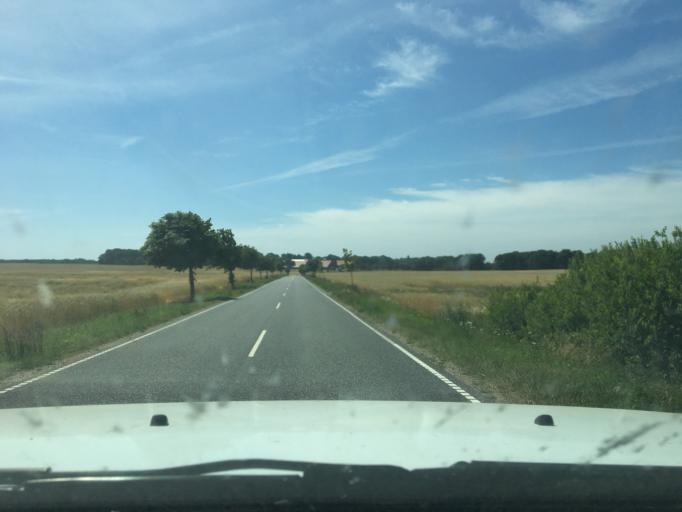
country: DK
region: Central Jutland
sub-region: Viborg Kommune
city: Bjerringbro
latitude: 56.5165
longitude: 9.6250
